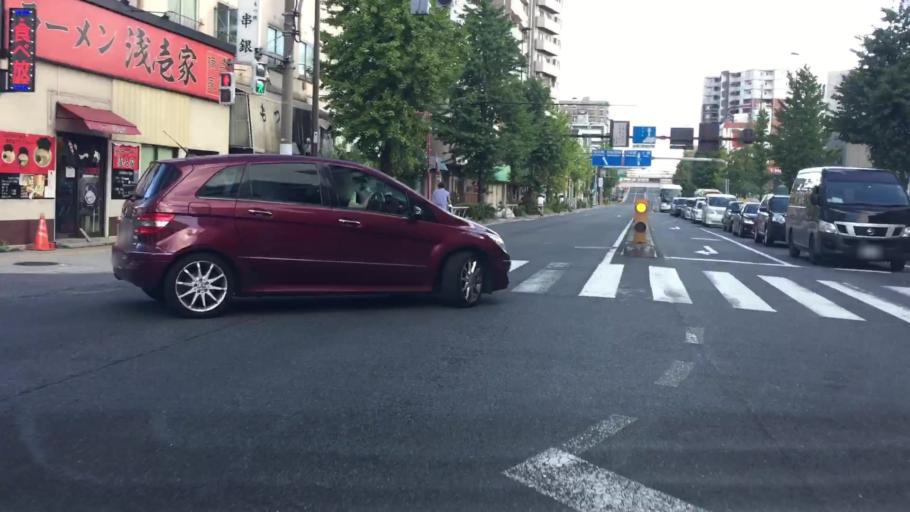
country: JP
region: Saitama
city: Soka
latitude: 35.7687
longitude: 139.8036
